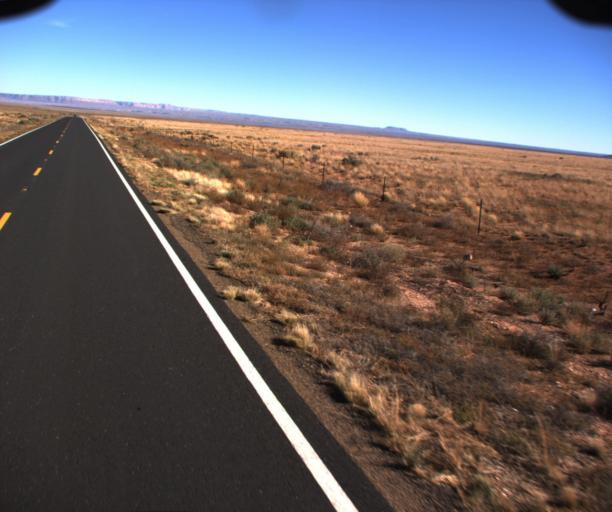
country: US
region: Arizona
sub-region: Coconino County
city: Fredonia
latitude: 36.7223
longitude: -112.0172
